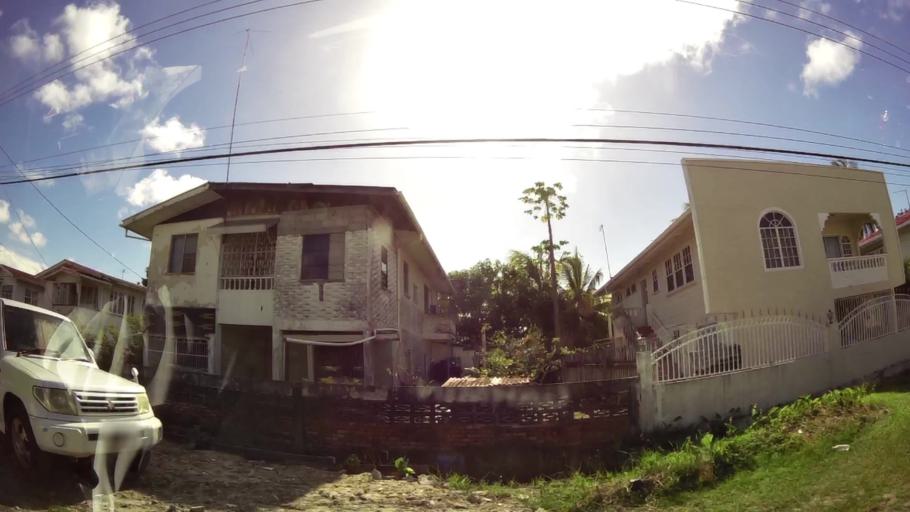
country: GY
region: Demerara-Mahaica
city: Georgetown
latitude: 6.8154
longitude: -58.1297
